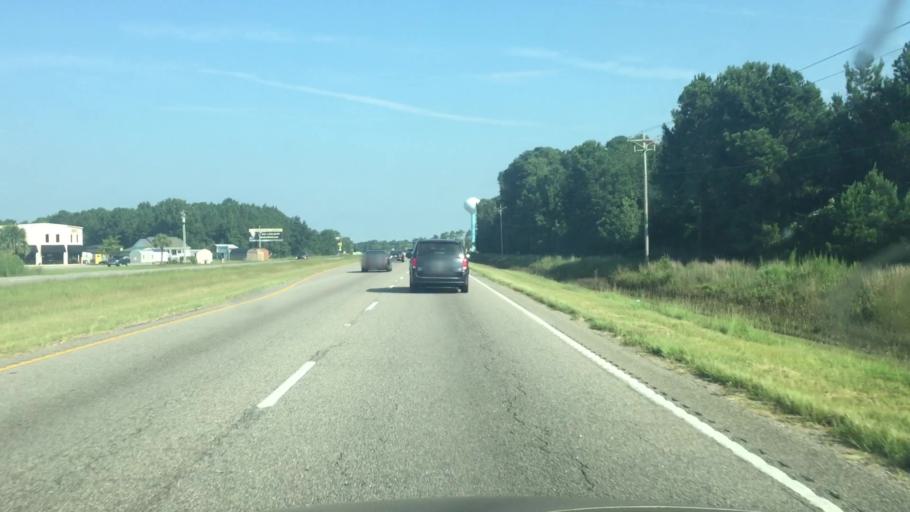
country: US
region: South Carolina
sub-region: Horry County
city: North Myrtle Beach
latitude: 33.8960
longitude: -78.6953
